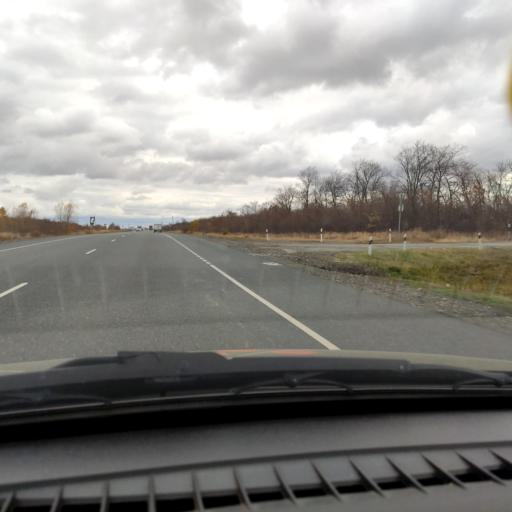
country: RU
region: Samara
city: Obsharovka
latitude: 53.2370
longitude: 48.9511
